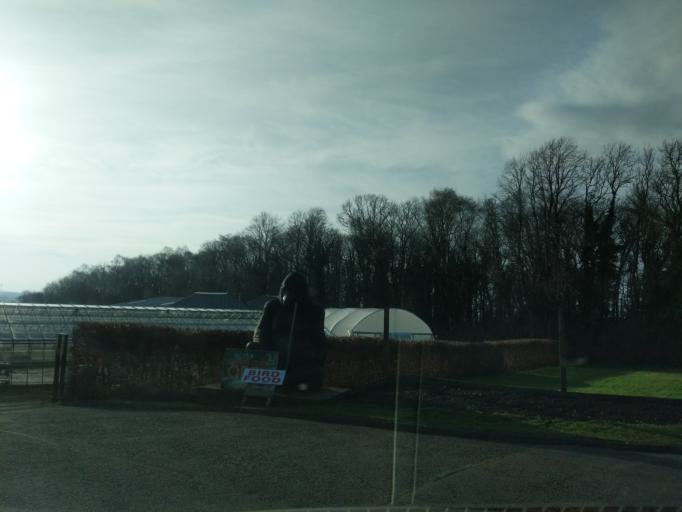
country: GB
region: Scotland
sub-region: South Lanarkshire
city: Law
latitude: 55.7323
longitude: -3.8848
